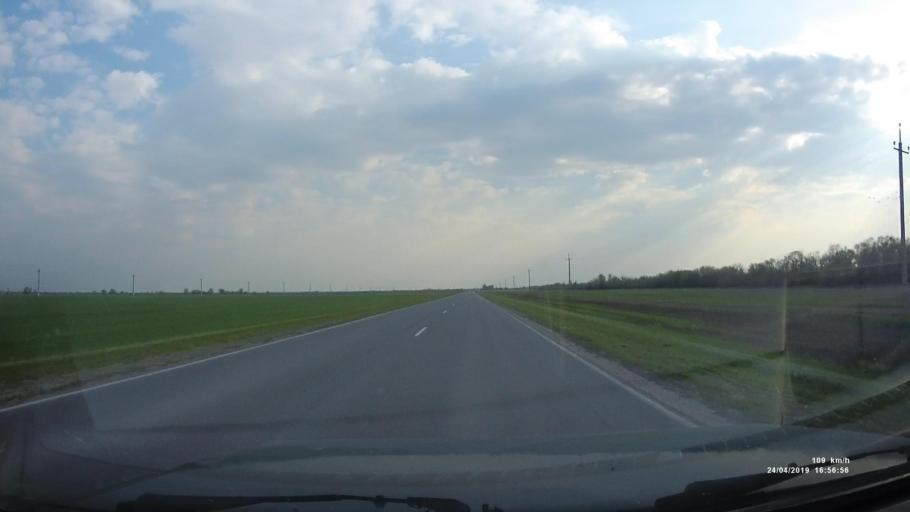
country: RU
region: Rostov
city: Proletarsk
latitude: 46.6443
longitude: 41.6732
